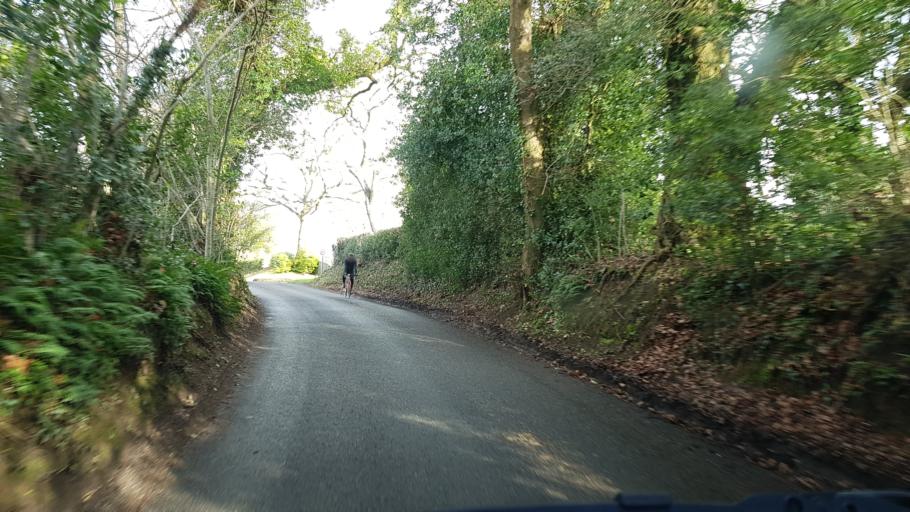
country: GB
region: England
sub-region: Surrey
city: Churt
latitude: 51.1380
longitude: -0.7715
